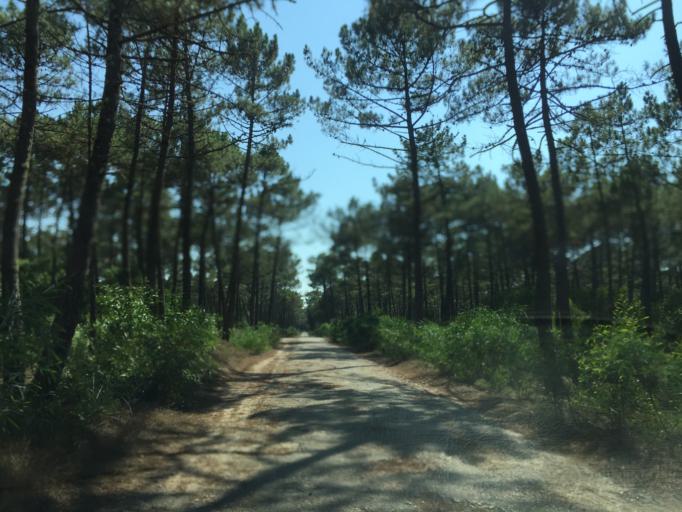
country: PT
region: Coimbra
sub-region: Figueira da Foz
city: Tavarede
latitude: 40.2450
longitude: -8.8456
